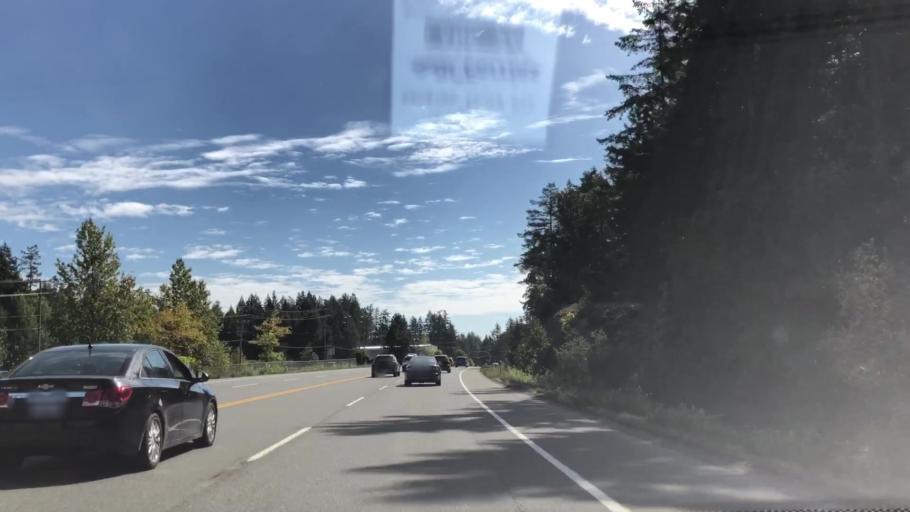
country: CA
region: British Columbia
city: Nanaimo
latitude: 49.1346
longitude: -123.8713
